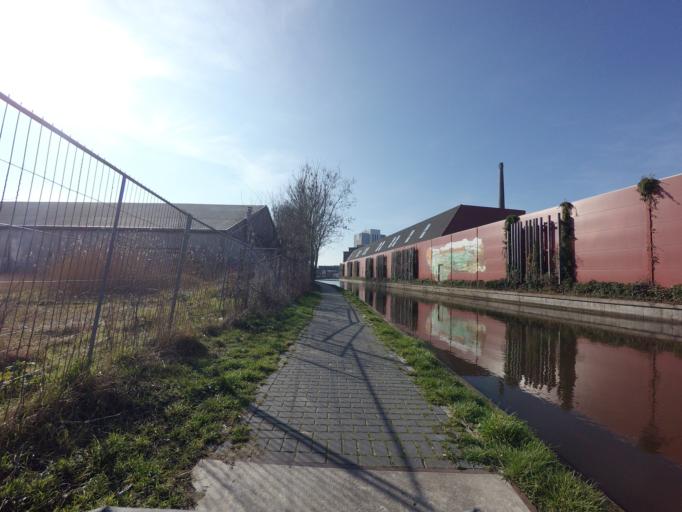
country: NL
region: Utrecht
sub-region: Gemeente Woerden
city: Woerden
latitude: 52.0856
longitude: 4.8716
